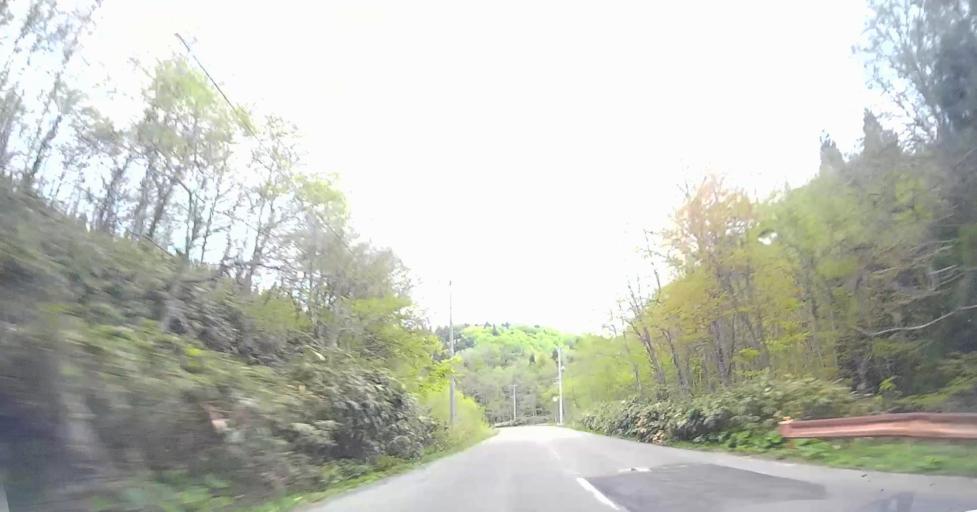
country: JP
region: Aomori
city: Goshogawara
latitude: 41.1150
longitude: 140.5287
